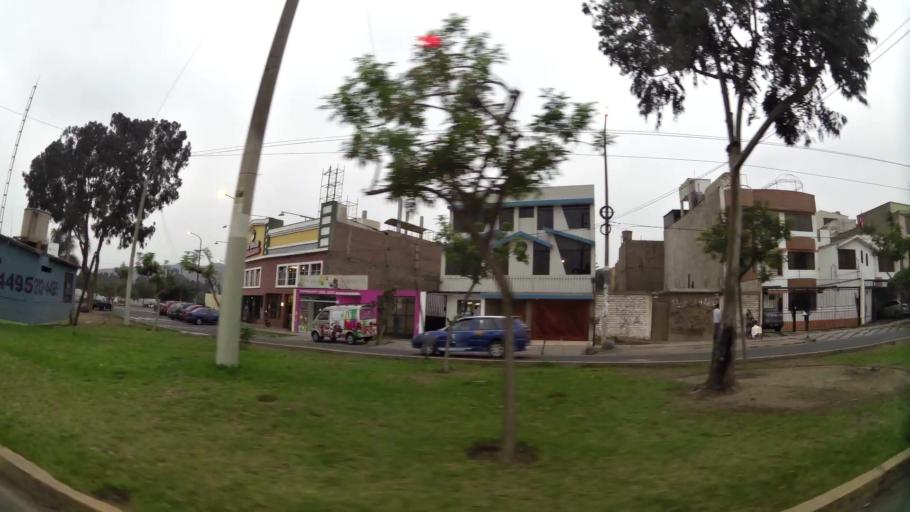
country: PE
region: Lima
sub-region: Lima
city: La Molina
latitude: -12.1008
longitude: -76.9429
